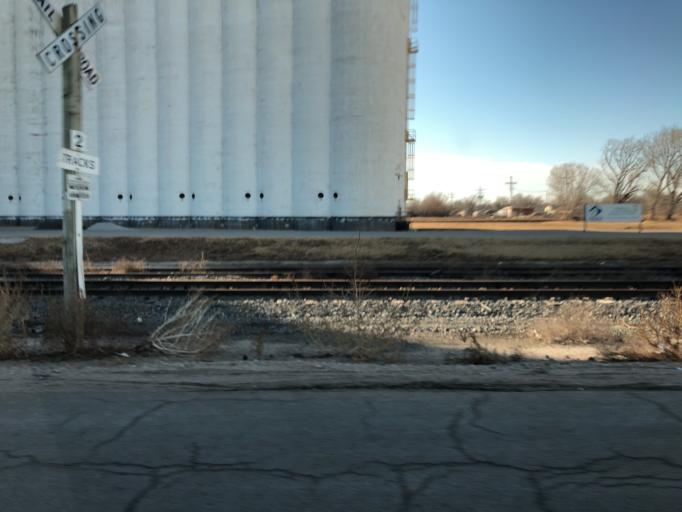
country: US
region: Kansas
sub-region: Reno County
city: Hutchinson
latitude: 38.0536
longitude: -97.8854
